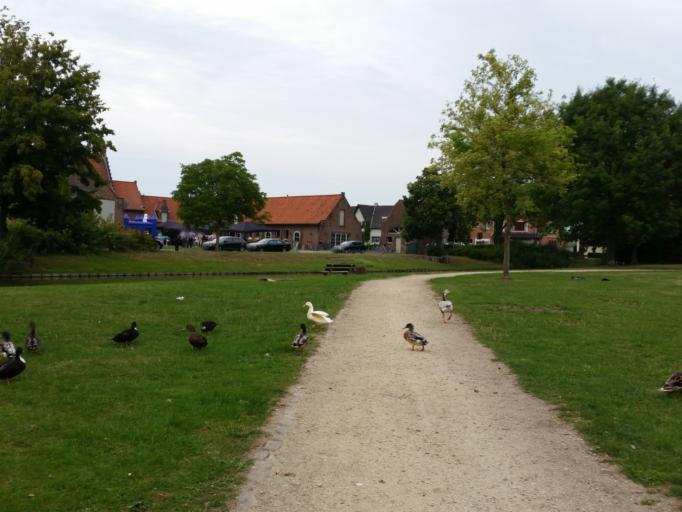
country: BE
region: Flanders
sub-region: Provincie Vlaams-Brabant
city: Zemst
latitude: 50.9651
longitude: 4.4492
